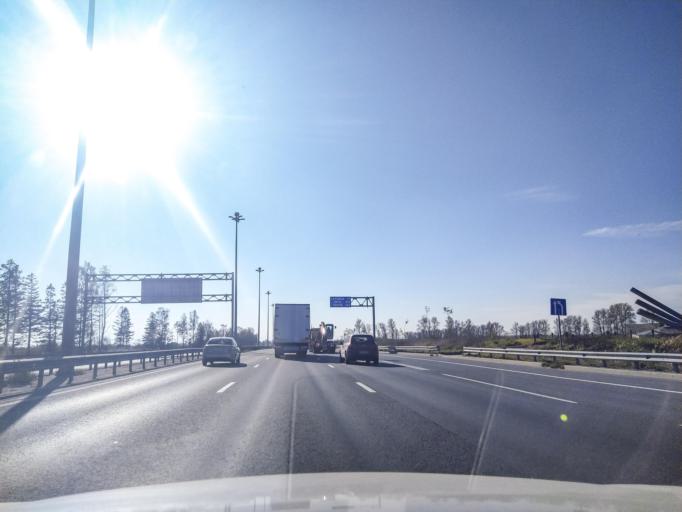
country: RU
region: Leningrad
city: Maloye Verevo
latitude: 59.6790
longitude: 30.2414
